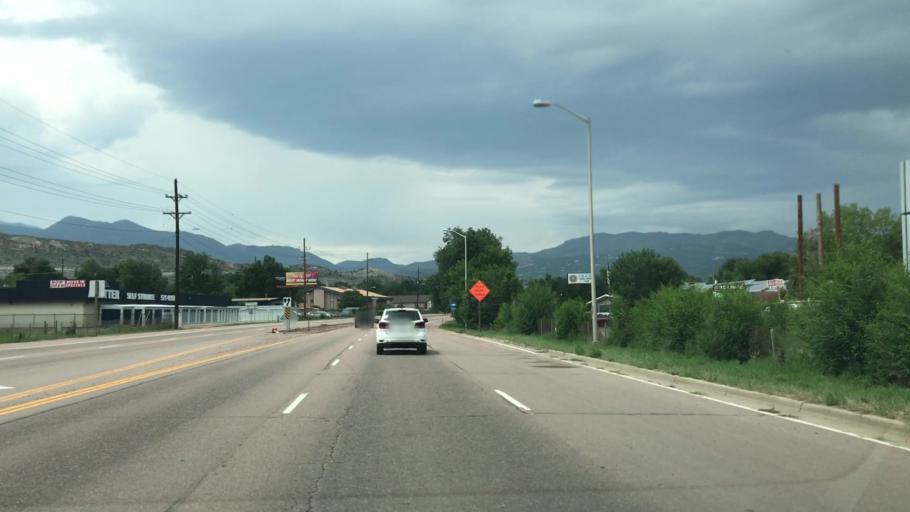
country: US
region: Colorado
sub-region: El Paso County
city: Colorado Springs
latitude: 38.8412
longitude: -104.8605
